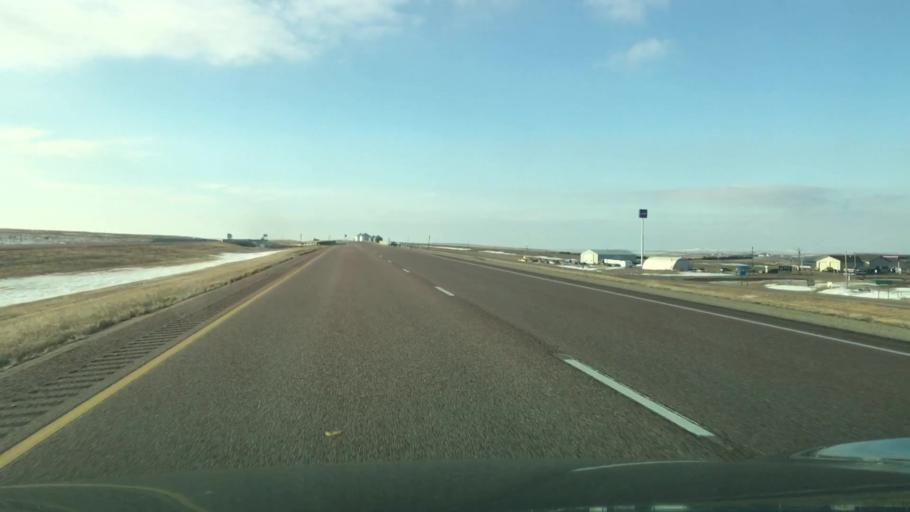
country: US
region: South Dakota
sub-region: Lyman County
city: Kennebec
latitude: 43.8948
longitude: -99.8633
